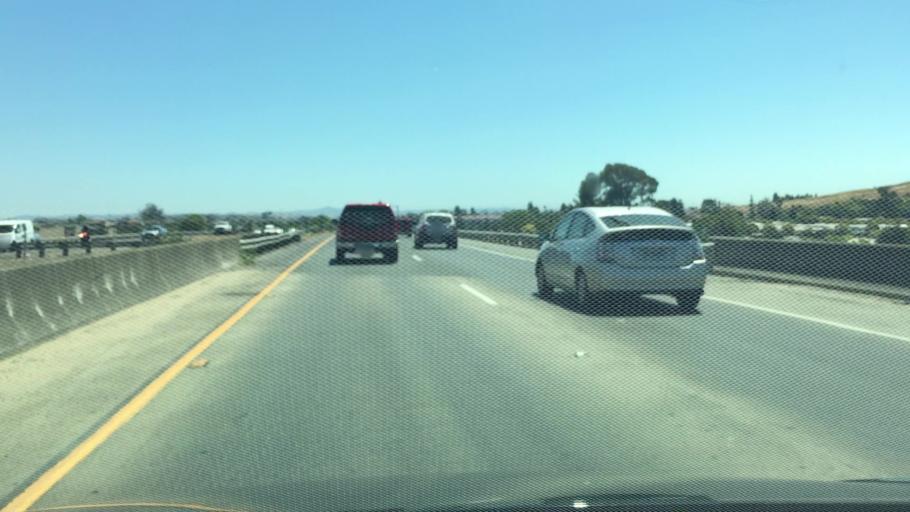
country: US
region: California
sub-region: Napa County
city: American Canyon
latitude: 38.1894
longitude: -122.2560
